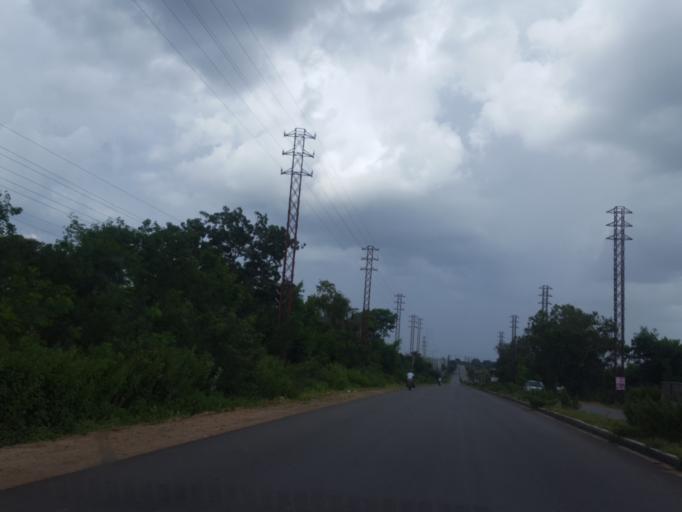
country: IN
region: Telangana
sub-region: Medak
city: Serilingampalle
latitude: 17.4186
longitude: 78.2342
